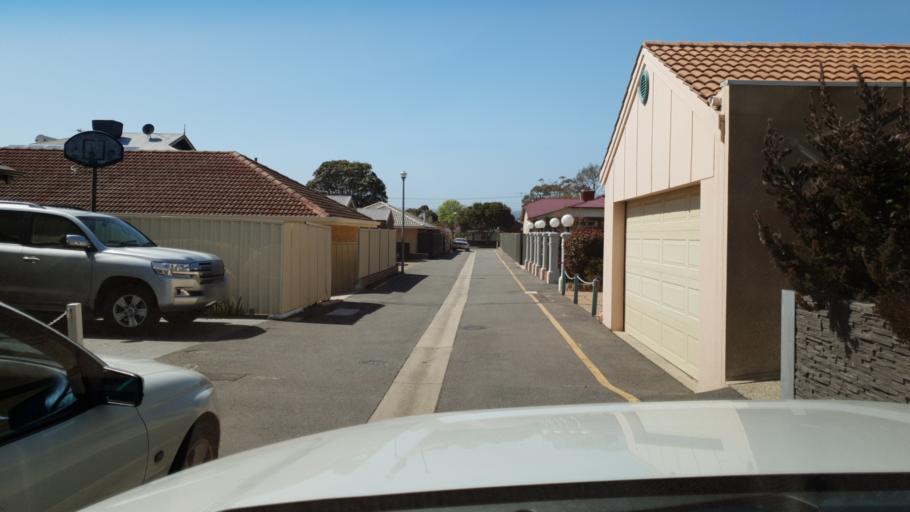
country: AU
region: South Australia
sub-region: Adelaide
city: Brighton
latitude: -35.0248
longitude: 138.5191
